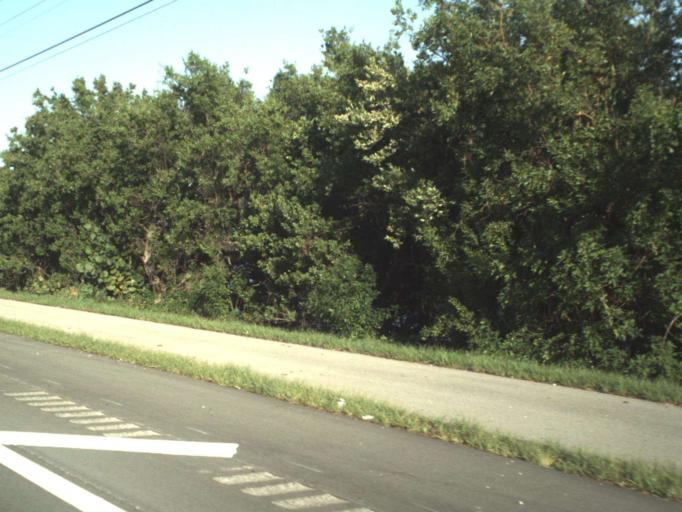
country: US
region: Florida
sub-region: Monroe County
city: Islamorada
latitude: 24.8384
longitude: -80.7960
